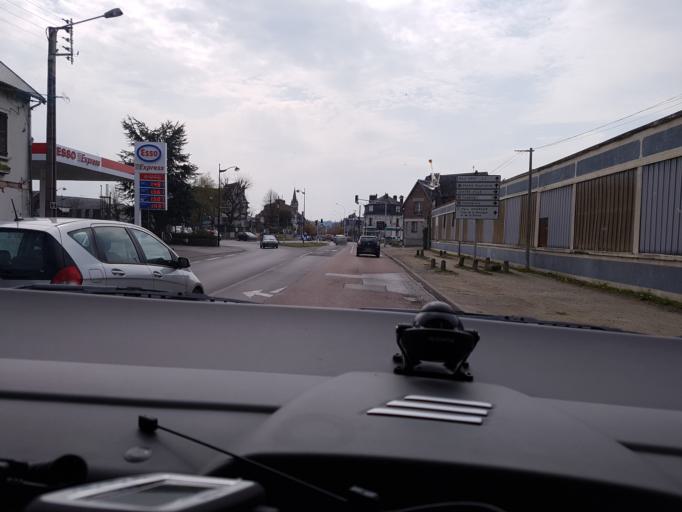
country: FR
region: Picardie
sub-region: Departement de l'Aisne
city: Soissons
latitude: 49.3867
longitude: 3.3329
